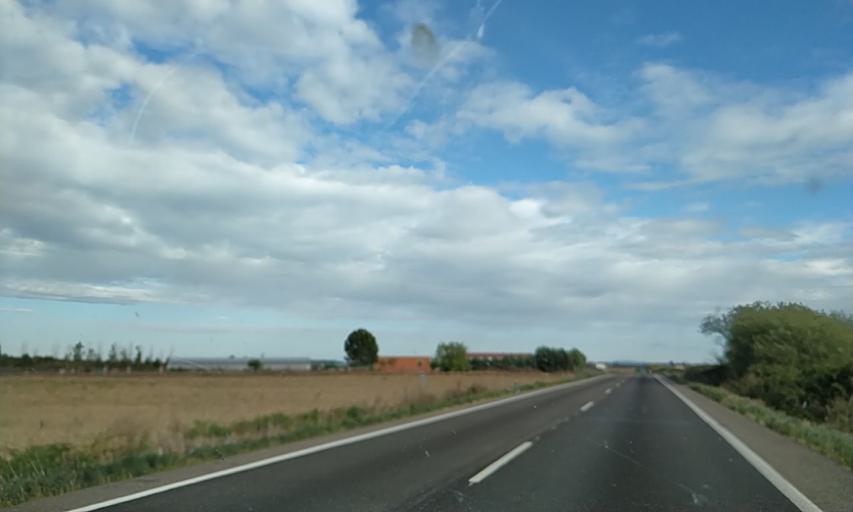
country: ES
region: Extremadura
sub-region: Provincia de Caceres
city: Moraleja
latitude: 40.0525
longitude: -6.6415
